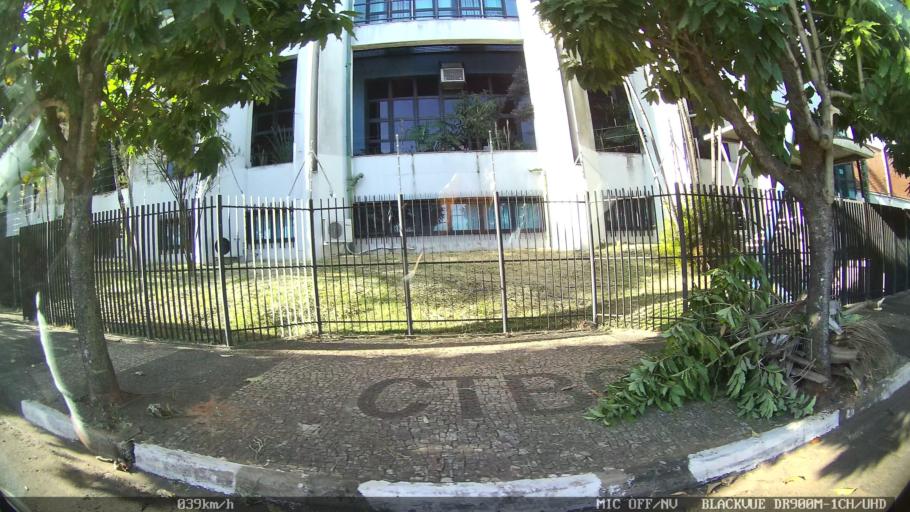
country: BR
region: Sao Paulo
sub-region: Franca
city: Franca
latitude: -20.5187
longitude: -47.3817
